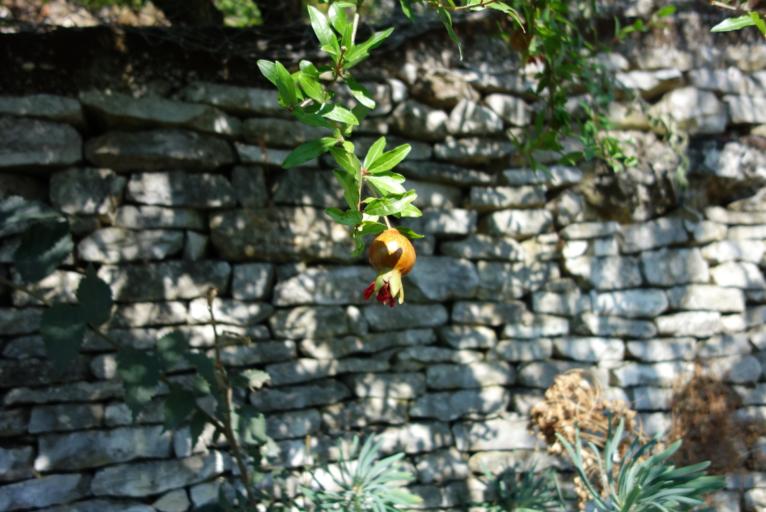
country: AL
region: Gjirokaster
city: Gjirokaster
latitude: 40.0723
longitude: 20.1357
